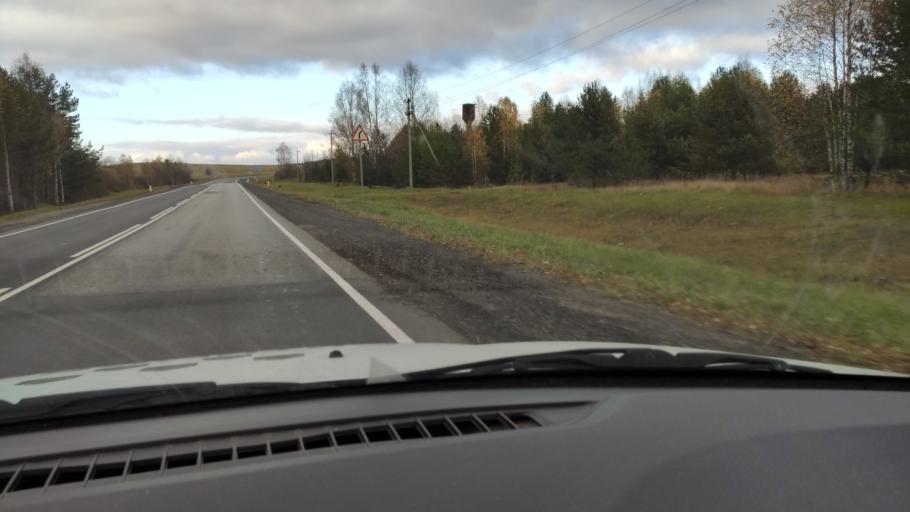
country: RU
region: Kirov
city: Belaya Kholunitsa
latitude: 58.8882
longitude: 50.8749
